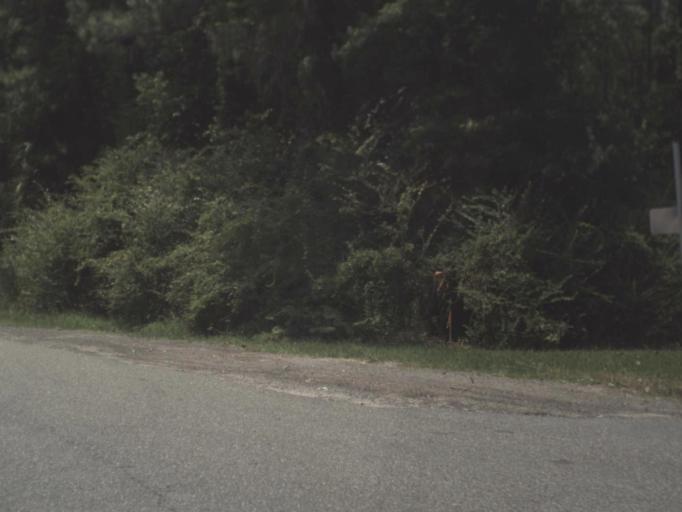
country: US
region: Florida
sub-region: Duval County
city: Baldwin
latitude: 30.2936
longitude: -81.9831
